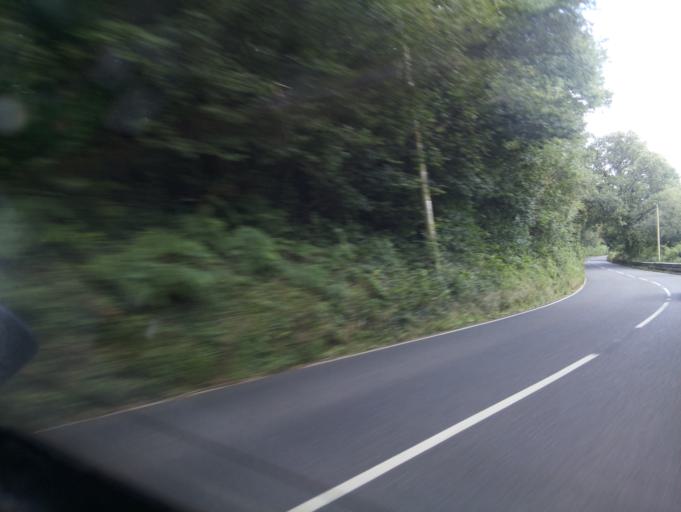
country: GB
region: England
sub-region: Devon
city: Ottery St Mary
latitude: 50.7425
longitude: -3.2098
